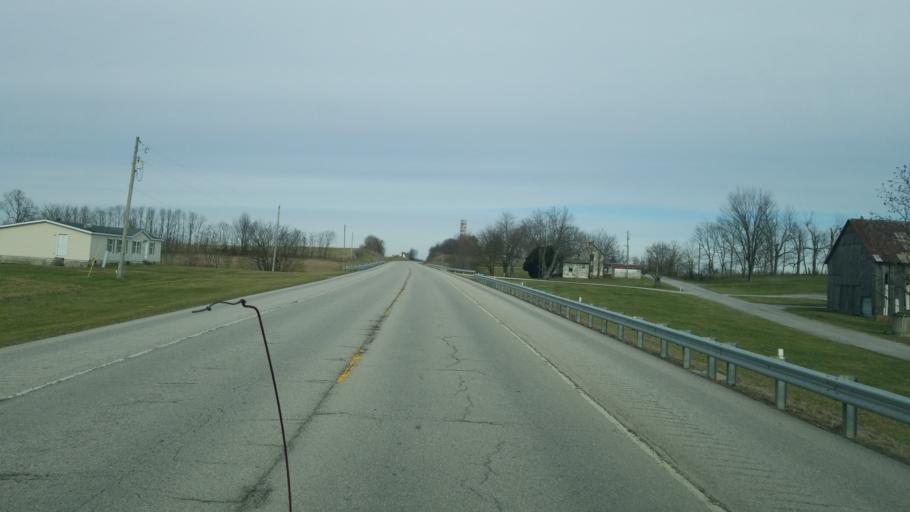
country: US
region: Kentucky
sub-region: Fleming County
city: Flemingsburg
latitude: 38.4988
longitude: -83.8528
